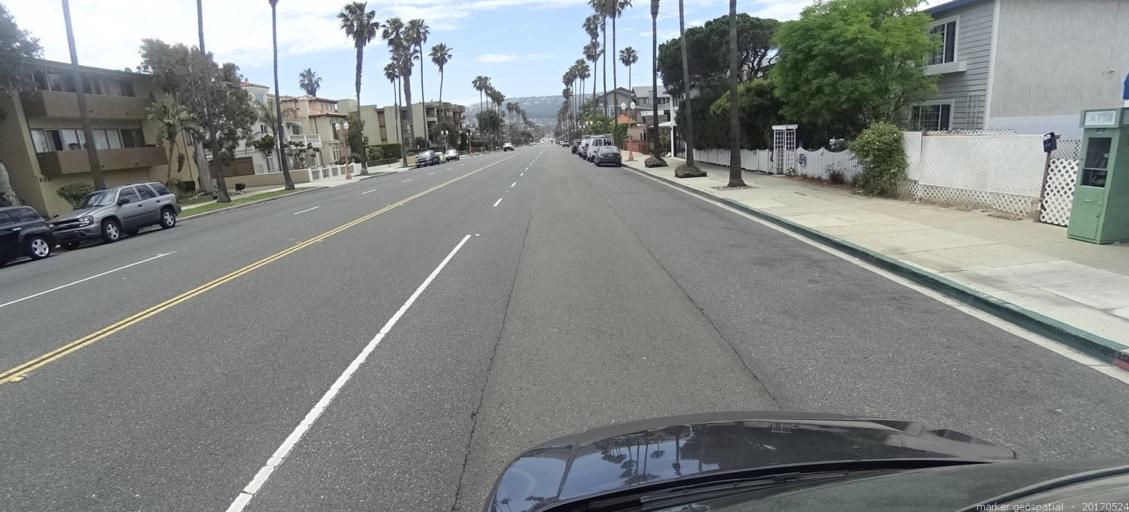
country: US
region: California
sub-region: Los Angeles County
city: Redondo Beach
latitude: 33.8276
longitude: -118.3888
